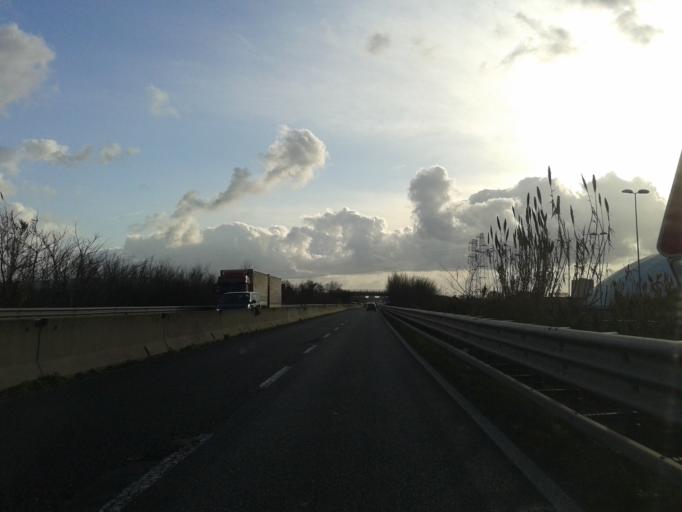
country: IT
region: Tuscany
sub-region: Provincia di Livorno
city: Livorno
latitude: 43.5574
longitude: 10.3447
